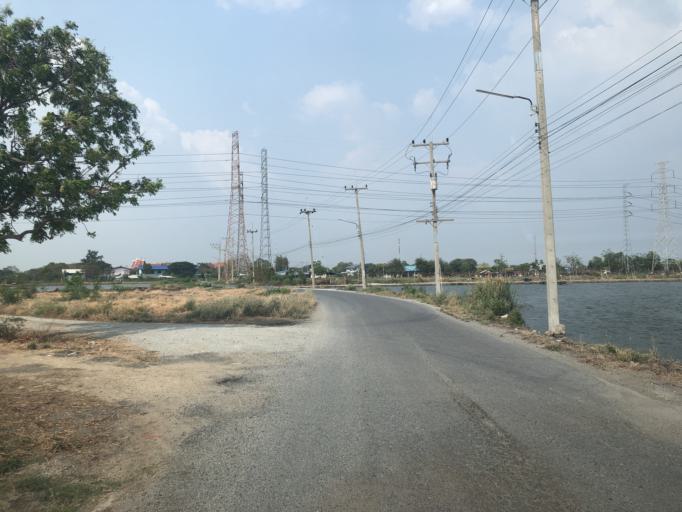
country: TH
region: Chachoengsao
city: Bang Pakong
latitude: 13.5182
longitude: 100.9394
